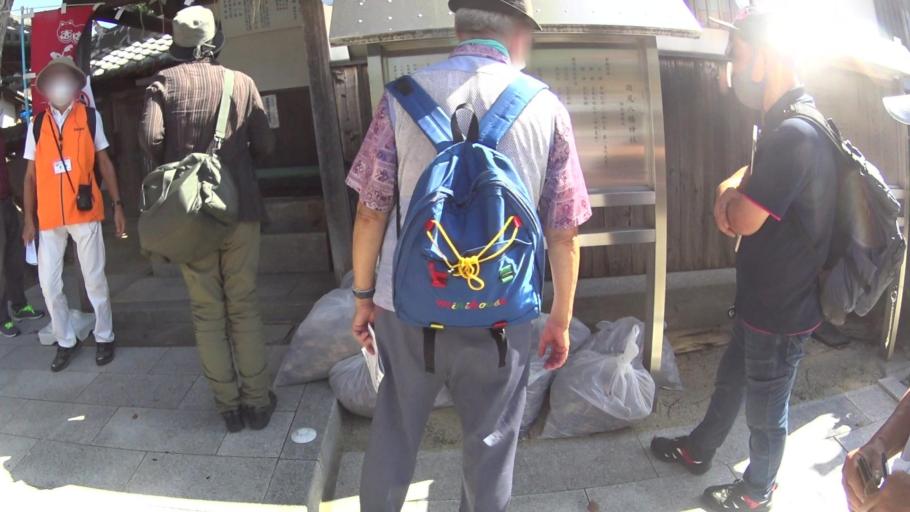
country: JP
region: Osaka
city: Matsubara
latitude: 34.5295
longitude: 135.5013
